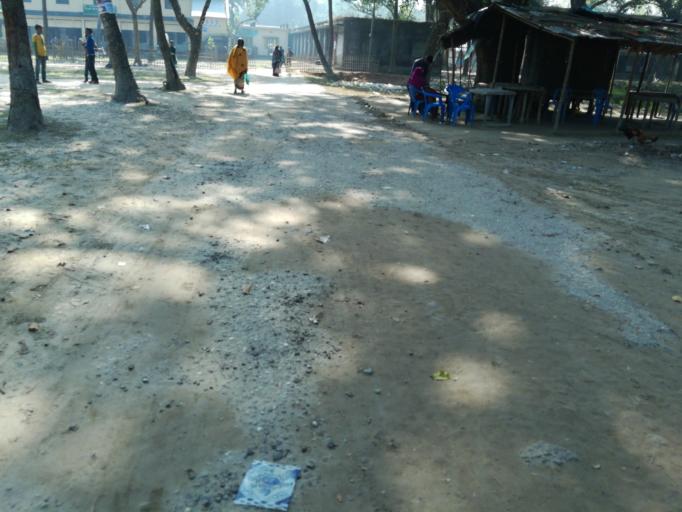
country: BD
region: Rangpur Division
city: Rangpur
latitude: 25.5688
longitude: 89.2734
